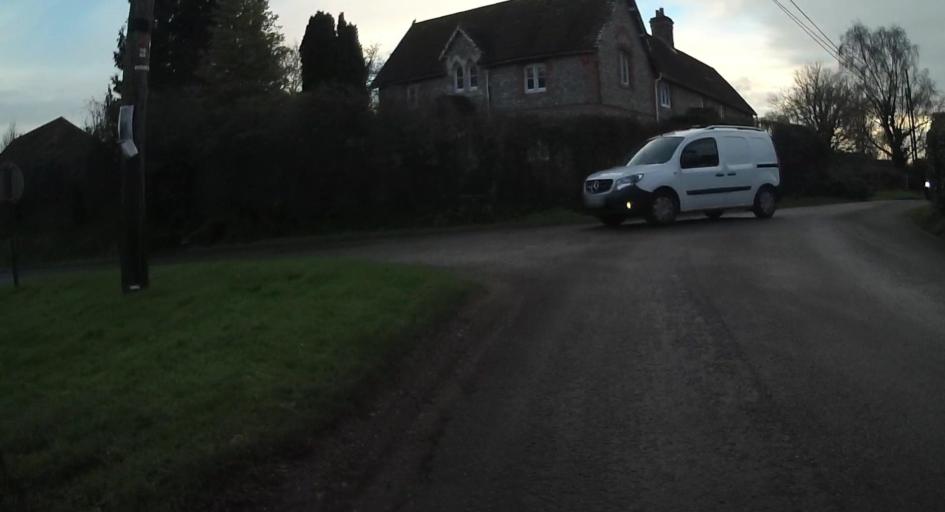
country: GB
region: England
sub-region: Hampshire
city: Swanmore
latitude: 51.0333
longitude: -1.1596
